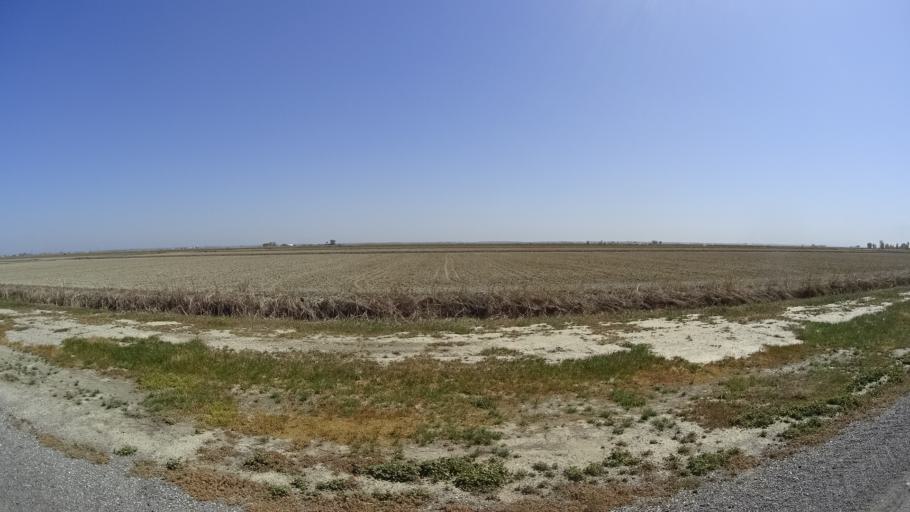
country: US
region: California
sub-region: Glenn County
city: Willows
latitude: 39.5159
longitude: -122.1027
